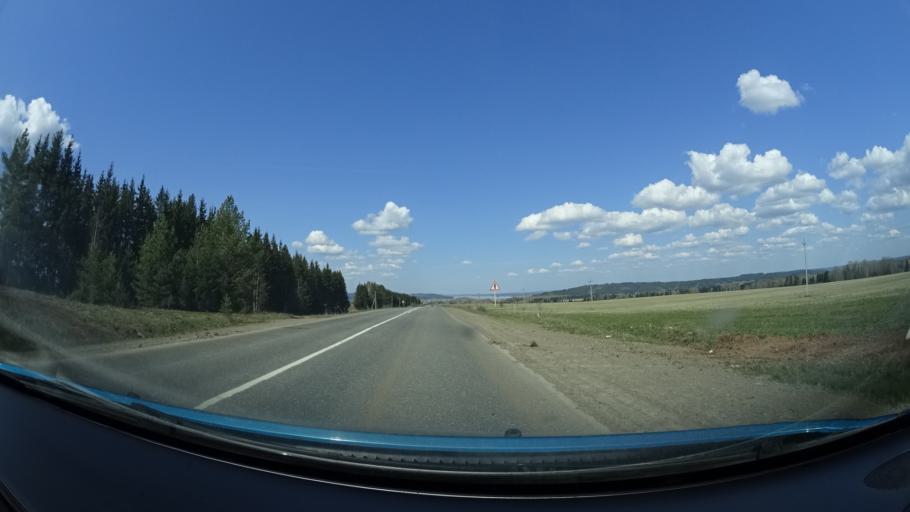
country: RU
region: Perm
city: Osa
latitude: 57.2680
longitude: 55.5722
